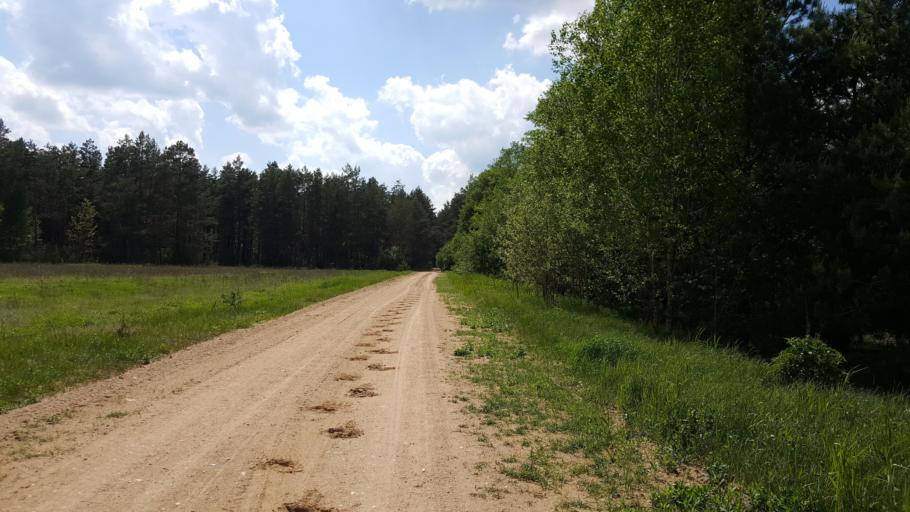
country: BY
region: Brest
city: Kamyanyets
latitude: 52.4422
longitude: 23.9823
